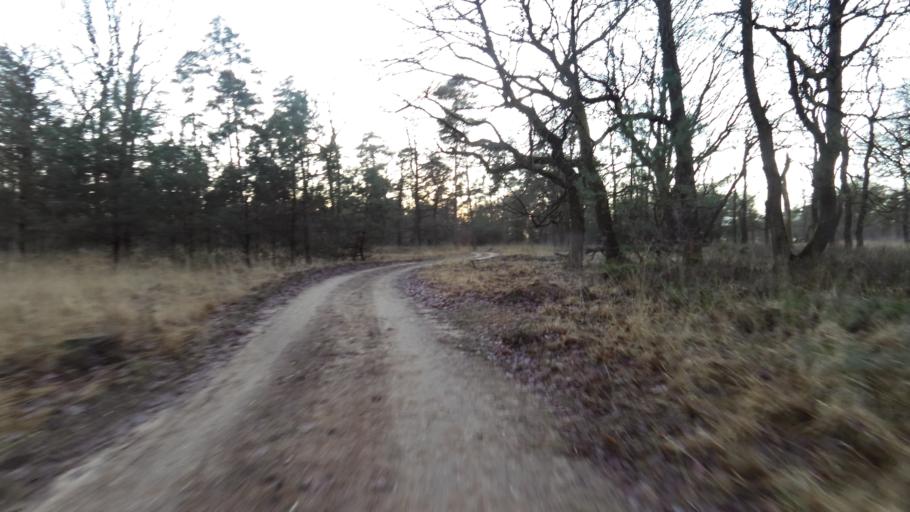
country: NL
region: Gelderland
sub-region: Gemeente Apeldoorn
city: Uddel
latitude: 52.2889
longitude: 5.8509
